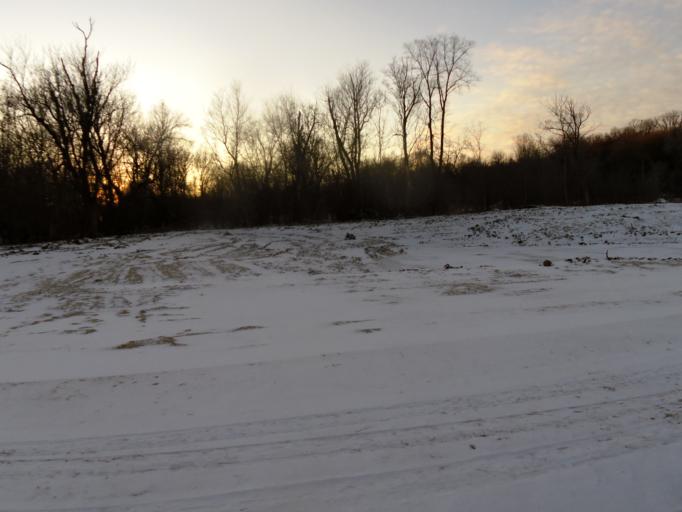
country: US
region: Minnesota
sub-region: Washington County
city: Lakeland
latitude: 44.9651
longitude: -92.8158
